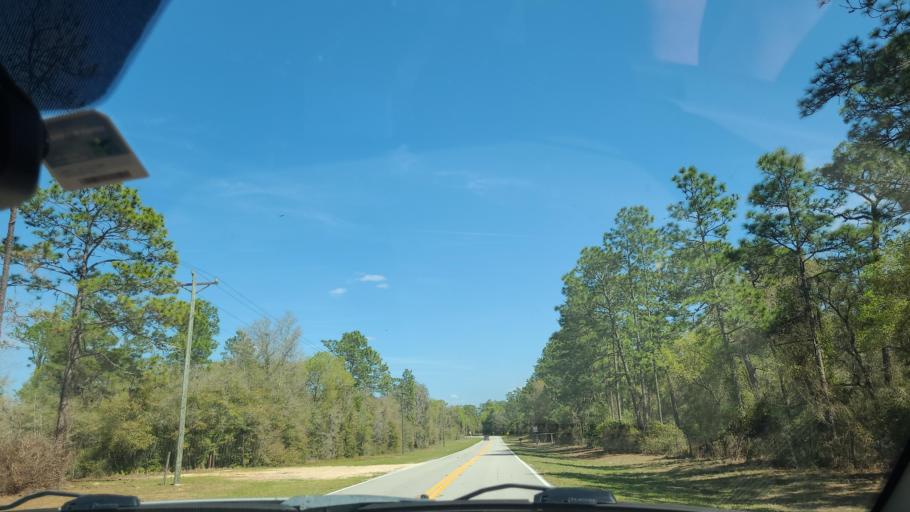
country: US
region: Florida
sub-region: Putnam County
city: Interlachen
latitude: 29.3781
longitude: -81.7781
